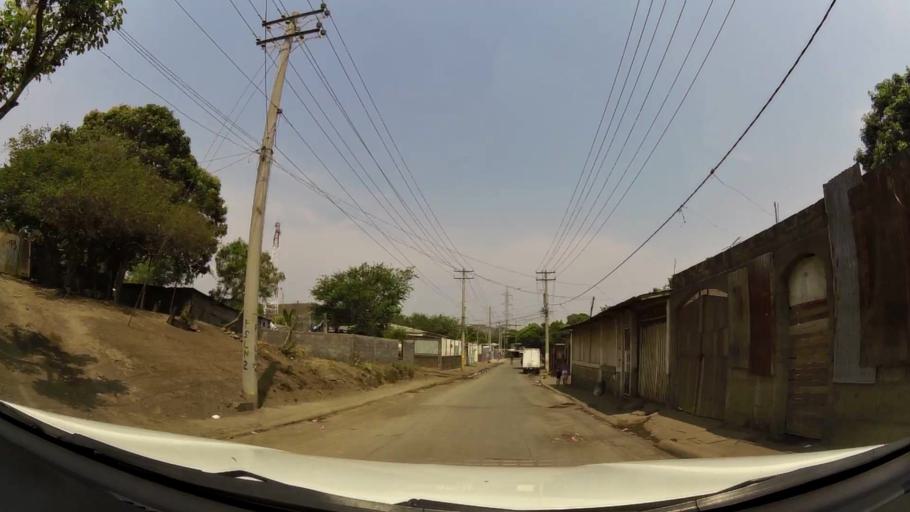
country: NI
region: Managua
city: Ciudad Sandino
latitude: 12.1590
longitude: -86.3094
